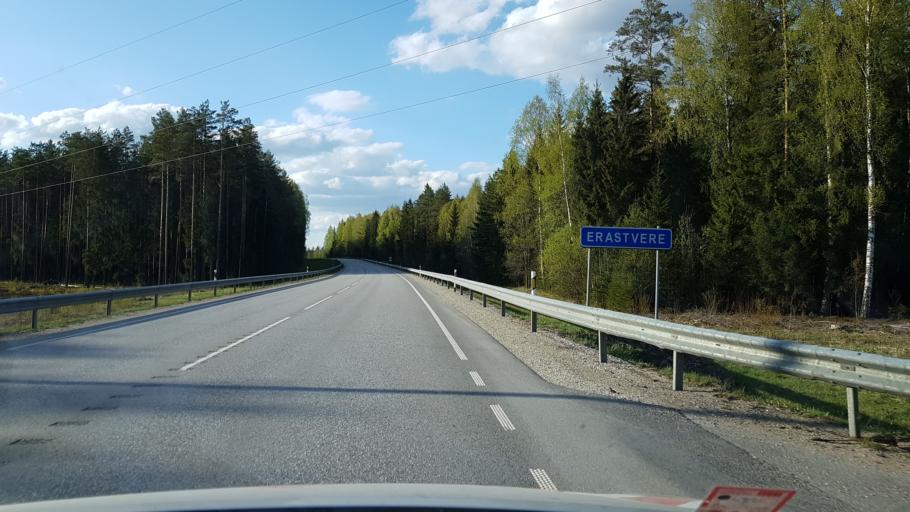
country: EE
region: Vorumaa
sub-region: Voru linn
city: Voru
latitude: 57.9630
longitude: 26.7915
